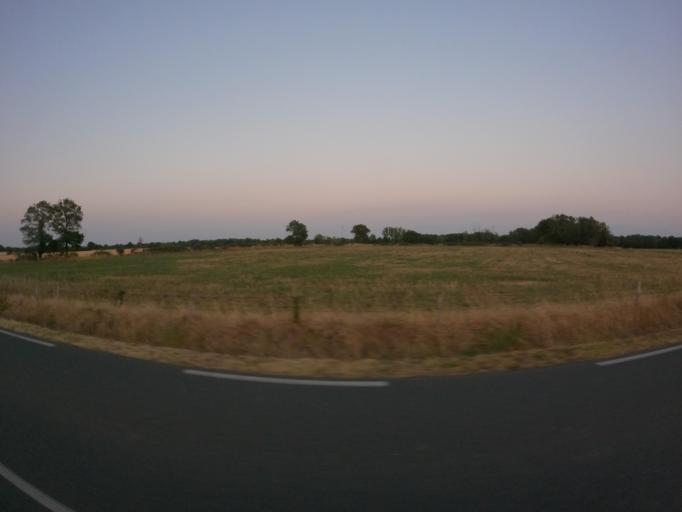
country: FR
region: Pays de la Loire
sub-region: Departement de Maine-et-Loire
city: Cande
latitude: 47.5814
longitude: -1.0118
